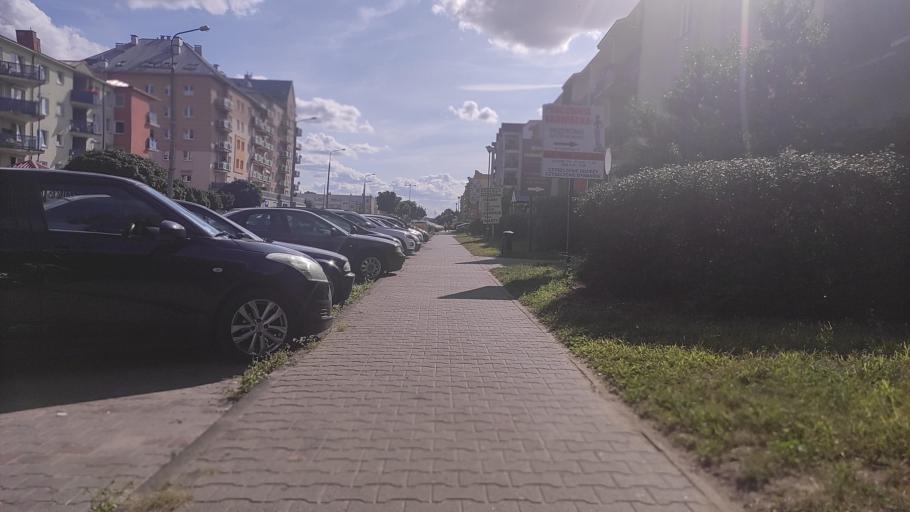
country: PL
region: Greater Poland Voivodeship
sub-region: Powiat poznanski
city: Swarzedz
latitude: 52.4008
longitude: 17.0658
